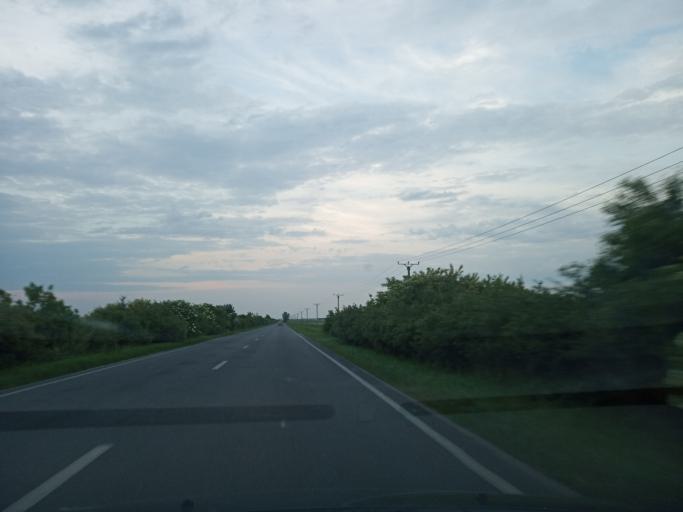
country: RO
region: Timis
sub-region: Oras Deta
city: Deta
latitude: 45.4282
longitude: 21.2304
